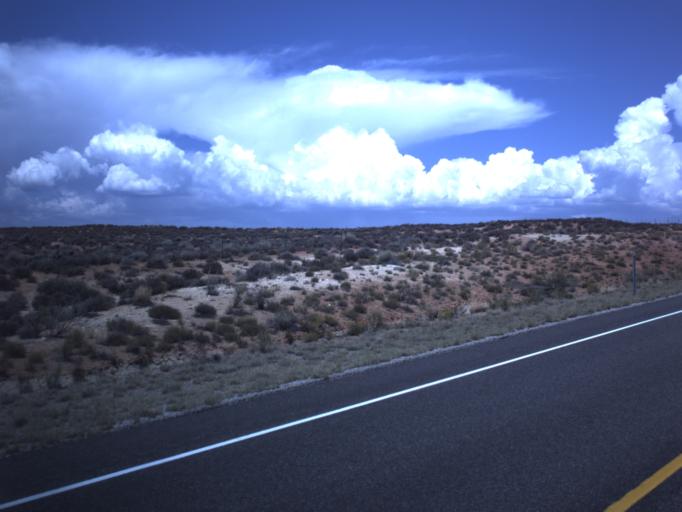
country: US
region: Utah
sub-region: San Juan County
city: Blanding
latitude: 37.3772
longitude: -109.5041
